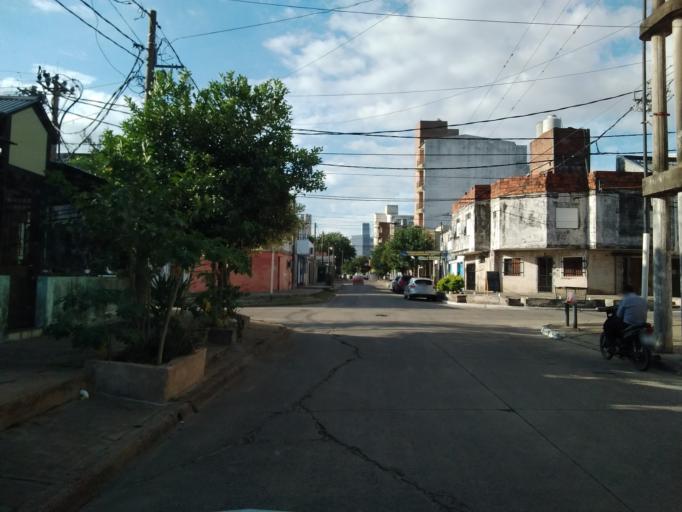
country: AR
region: Corrientes
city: Corrientes
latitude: -27.4645
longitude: -58.8219
